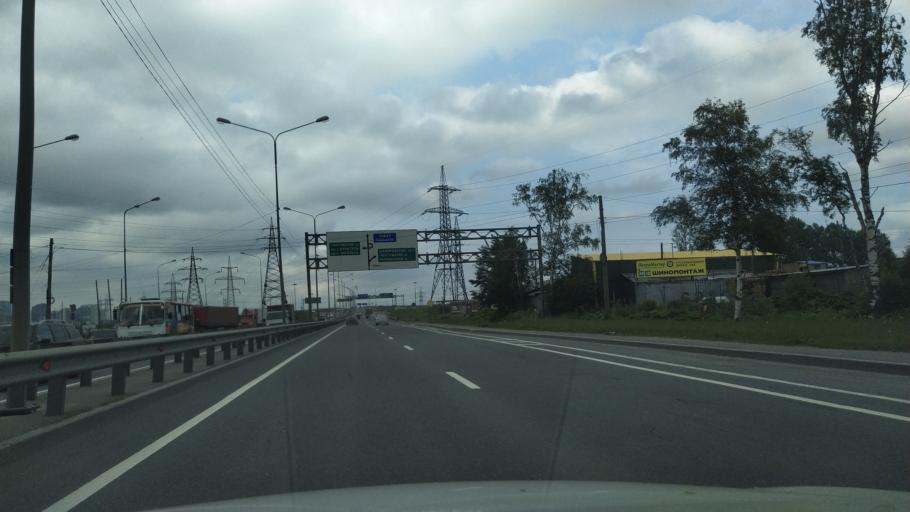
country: RU
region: Leningrad
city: Murino
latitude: 60.0120
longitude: 30.4551
